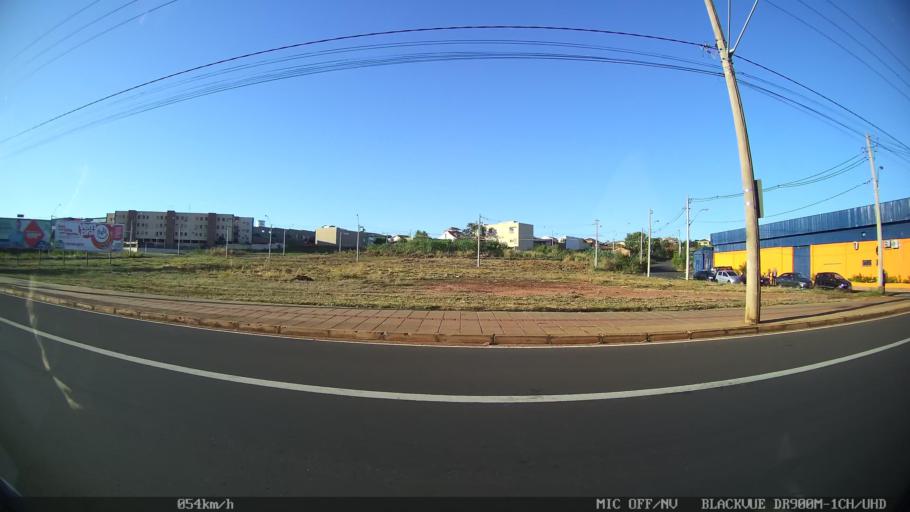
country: BR
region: Sao Paulo
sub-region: Sao Jose Do Rio Preto
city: Sao Jose do Rio Preto
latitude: -20.7840
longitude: -49.3781
